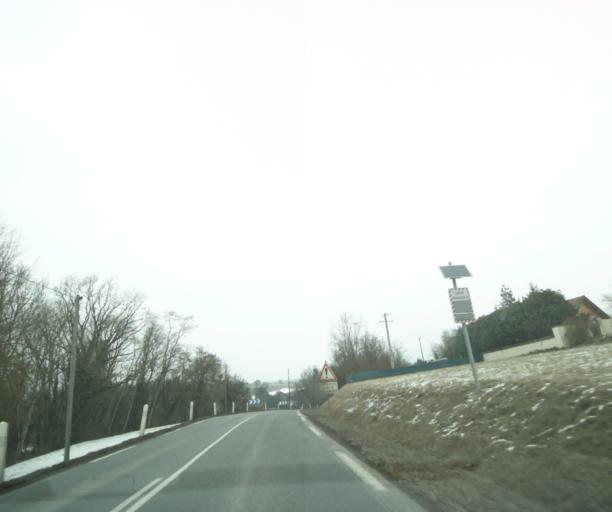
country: FR
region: Rhone-Alpes
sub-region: Departement de la Haute-Savoie
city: Contamine-sur-Arve
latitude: 46.1319
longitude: 6.3127
